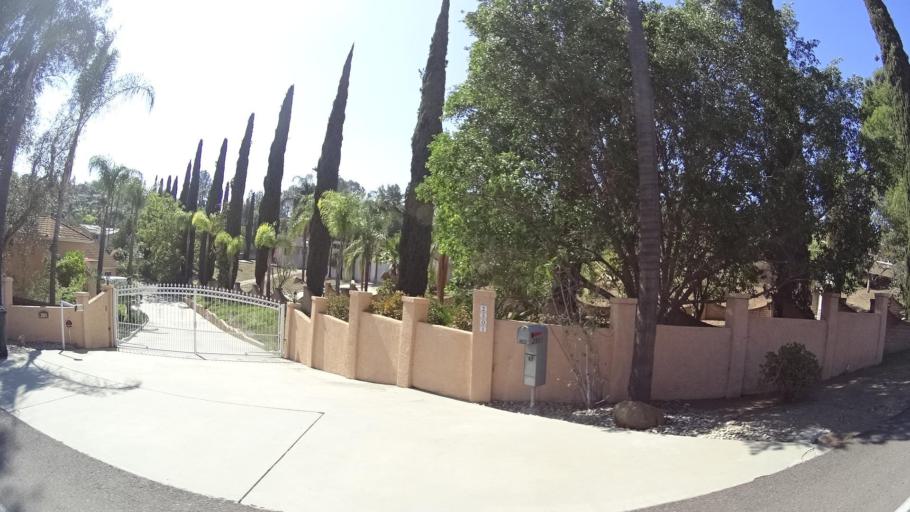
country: US
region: California
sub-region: San Diego County
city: Granite Hills
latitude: 32.7868
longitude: -116.8954
